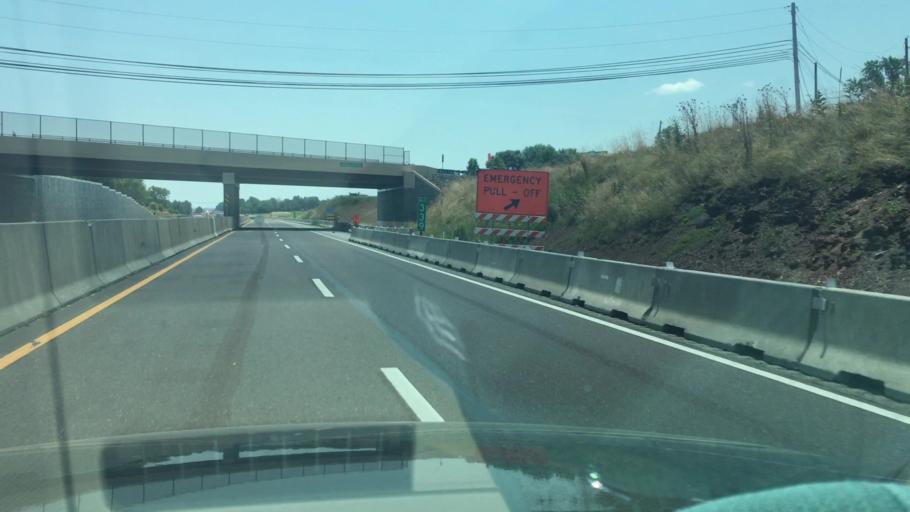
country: US
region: Pennsylvania
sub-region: Montgomery County
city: Harleysville
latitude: 40.3010
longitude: -75.3703
